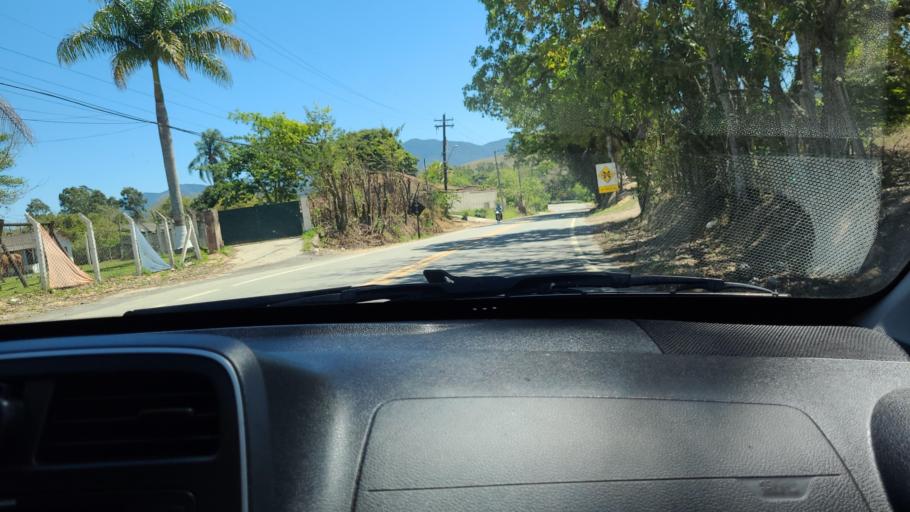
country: BR
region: Sao Paulo
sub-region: Tremembe
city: Tremembe
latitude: -22.8876
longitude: -45.5424
